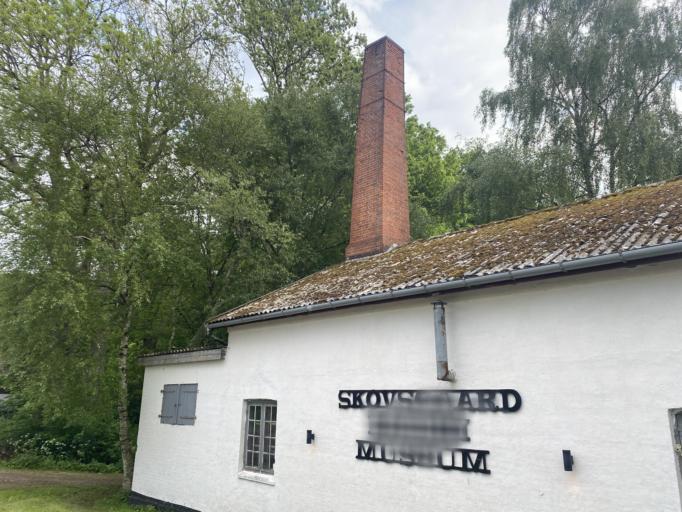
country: DK
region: Zealand
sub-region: Naestved Kommune
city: Fuglebjerg
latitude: 55.3430
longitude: 11.4841
